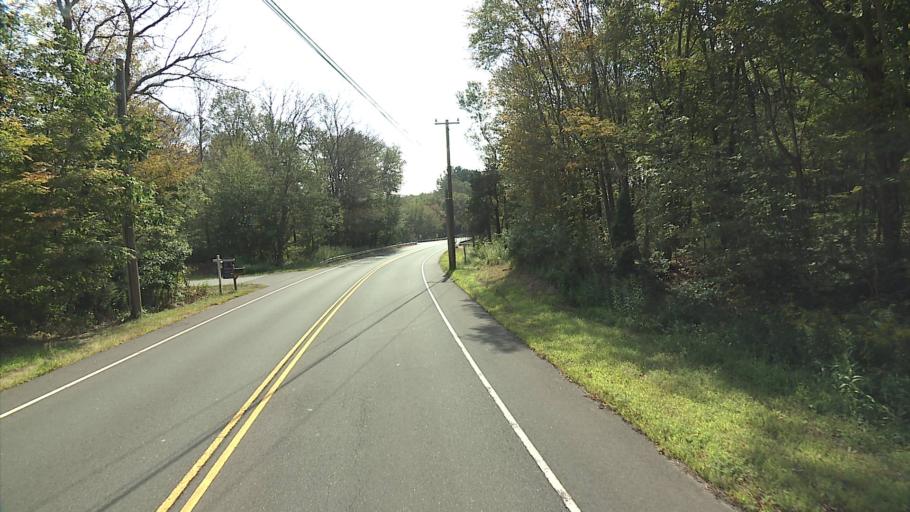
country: US
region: Connecticut
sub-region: Middlesex County
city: Durham
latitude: 41.4374
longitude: -72.6520
